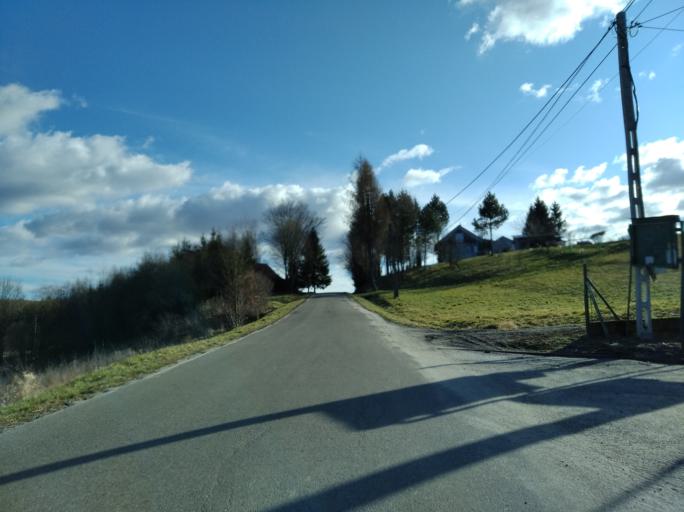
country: PL
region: Subcarpathian Voivodeship
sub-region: Powiat strzyzowski
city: Wisniowa
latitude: 49.8877
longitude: 21.7147
